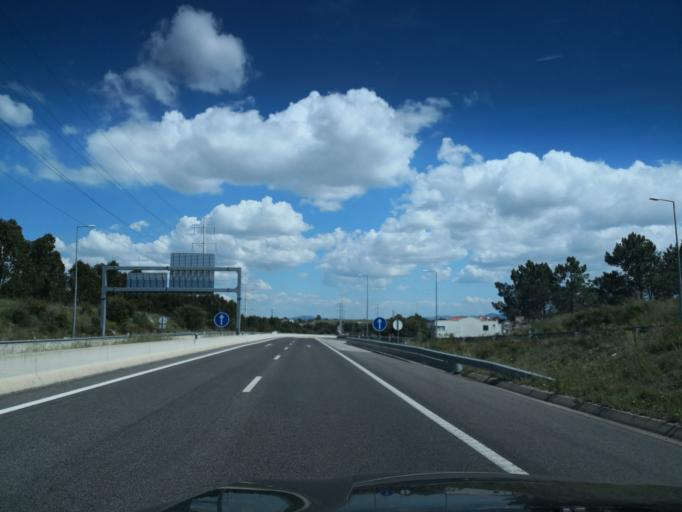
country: PT
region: Setubal
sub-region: Almada
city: Charneca
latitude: 38.6157
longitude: -9.1732
